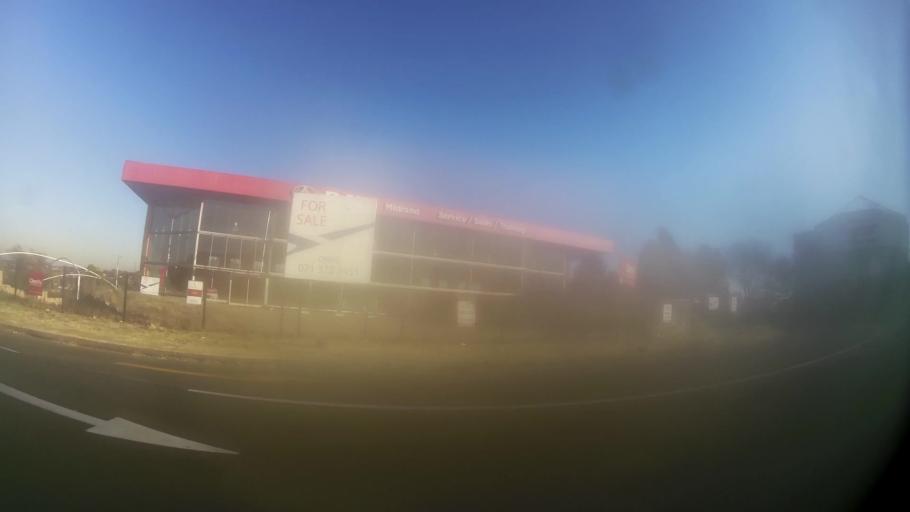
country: ZA
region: Gauteng
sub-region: City of Johannesburg Metropolitan Municipality
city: Midrand
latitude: -25.9887
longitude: 28.1308
